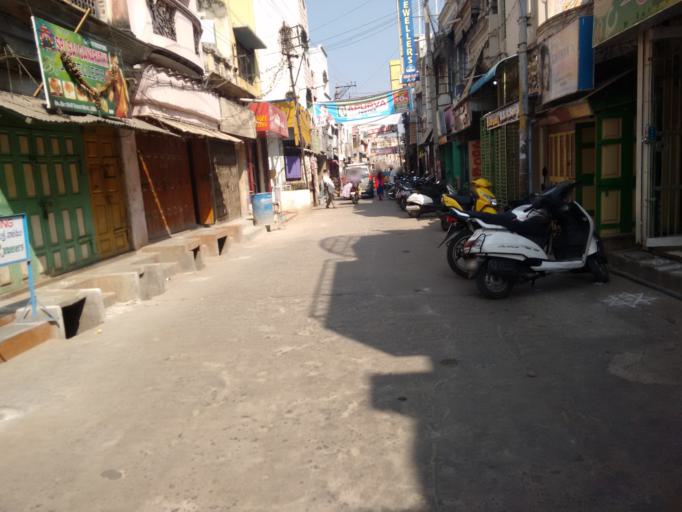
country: IN
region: Andhra Pradesh
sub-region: Chittoor
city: Chittoor
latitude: 13.2191
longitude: 79.0967
